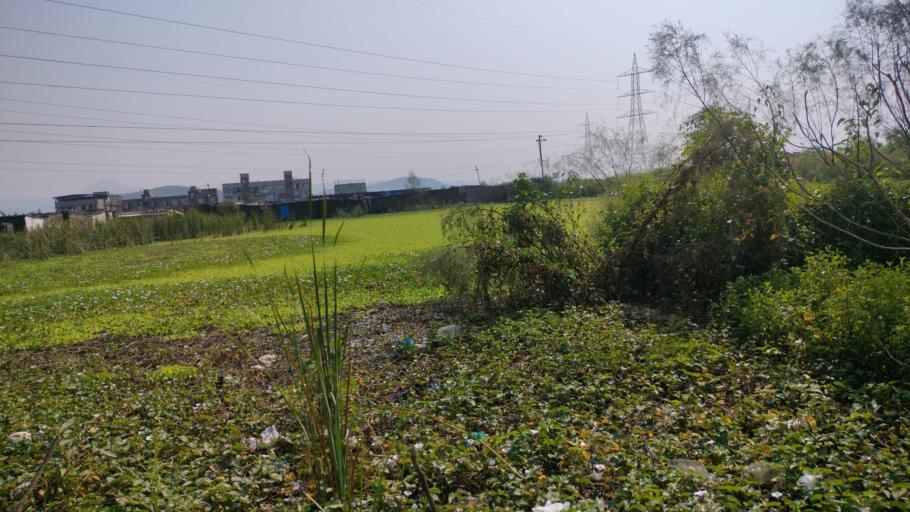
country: IN
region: Maharashtra
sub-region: Thane
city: Bhayandar
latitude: 19.3546
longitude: 72.8654
